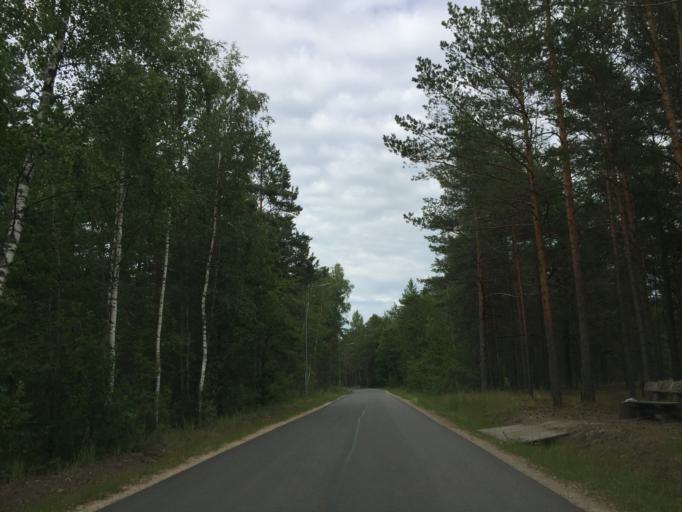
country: LV
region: Carnikava
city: Carnikava
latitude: 57.1320
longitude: 24.2565
